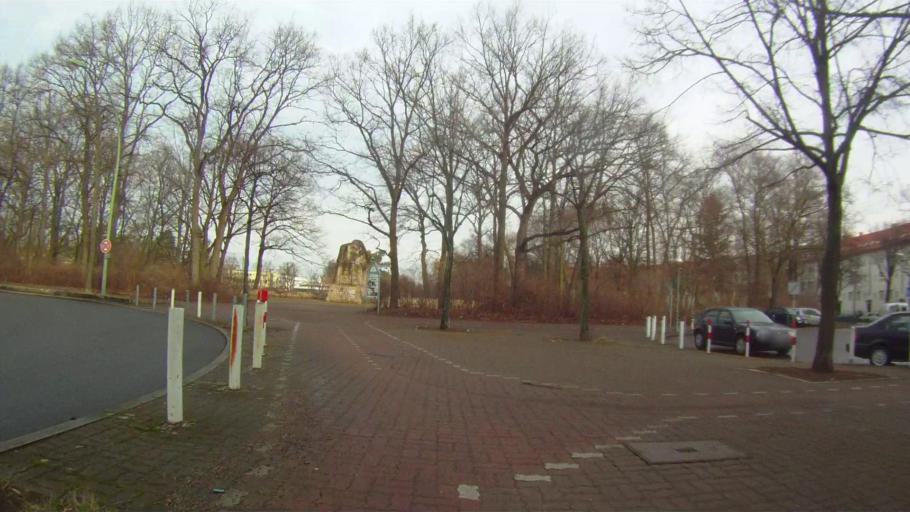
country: DE
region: Berlin
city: Schoneberg Bezirk
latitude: 52.4583
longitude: 13.3697
